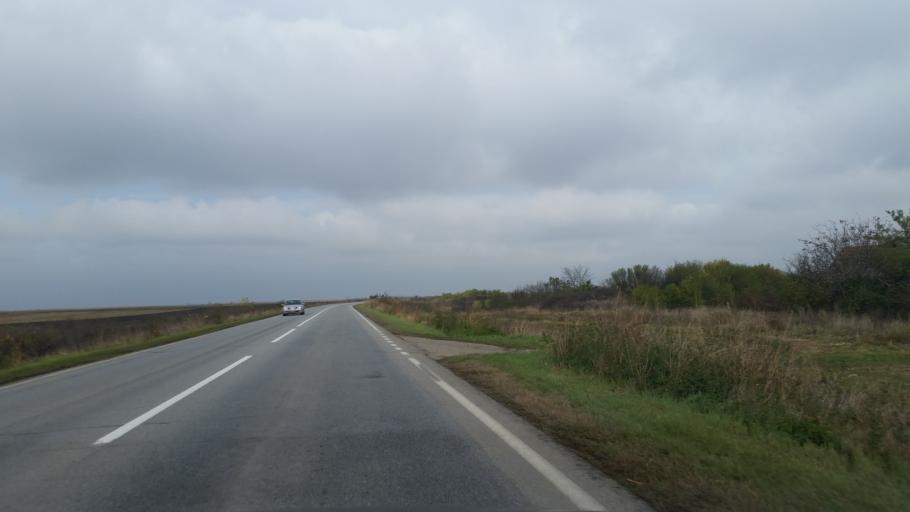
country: RS
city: Elemir
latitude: 45.4665
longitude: 20.3431
